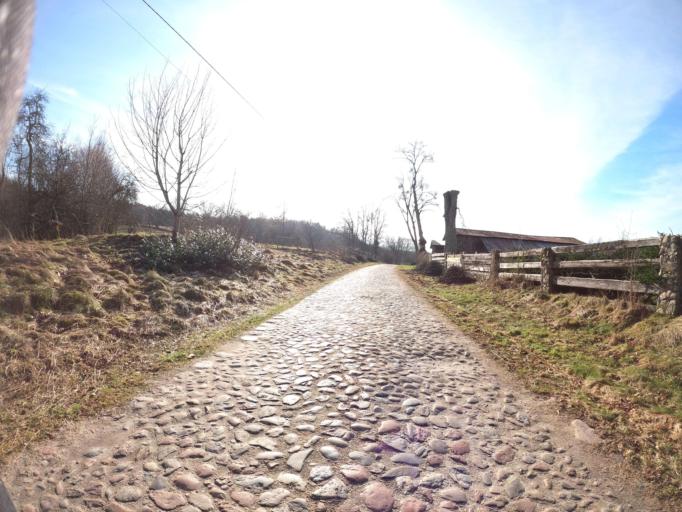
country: PL
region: West Pomeranian Voivodeship
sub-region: Powiat koszalinski
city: Polanow
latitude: 54.2358
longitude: 16.6432
